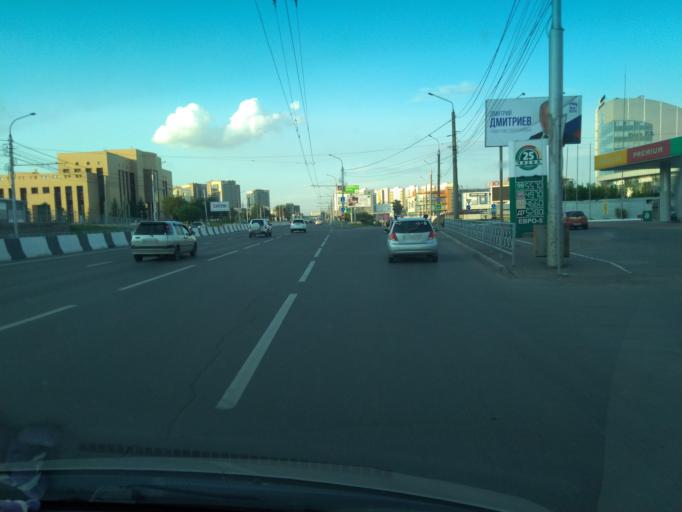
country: RU
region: Krasnoyarskiy
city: Krasnoyarsk
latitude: 56.0353
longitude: 92.9274
